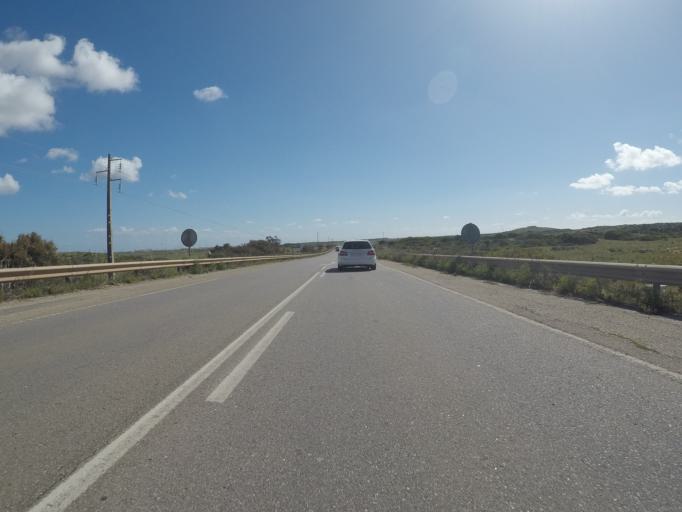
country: PT
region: Faro
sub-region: Vila do Bispo
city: Vila do Bispo
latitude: 37.0528
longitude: -8.9248
